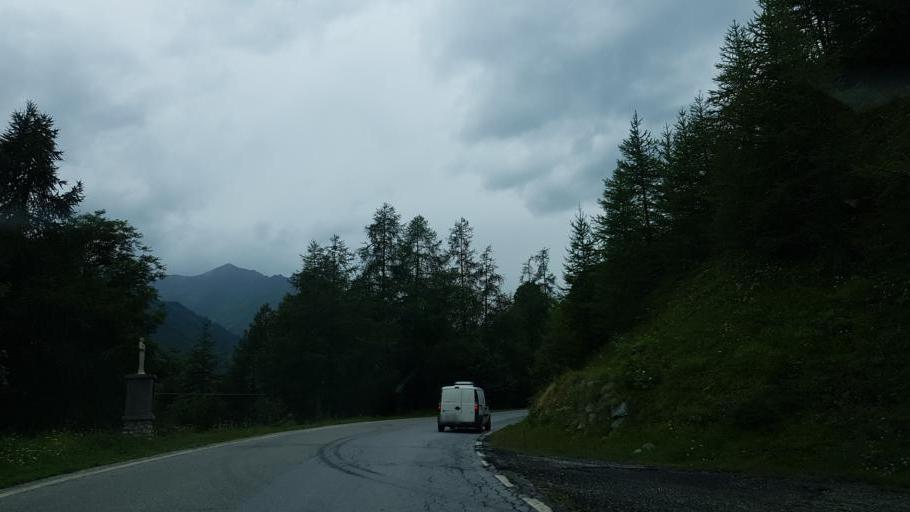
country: IT
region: Piedmont
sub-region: Provincia di Cuneo
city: Casteldelfino
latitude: 44.6097
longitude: 7.0581
